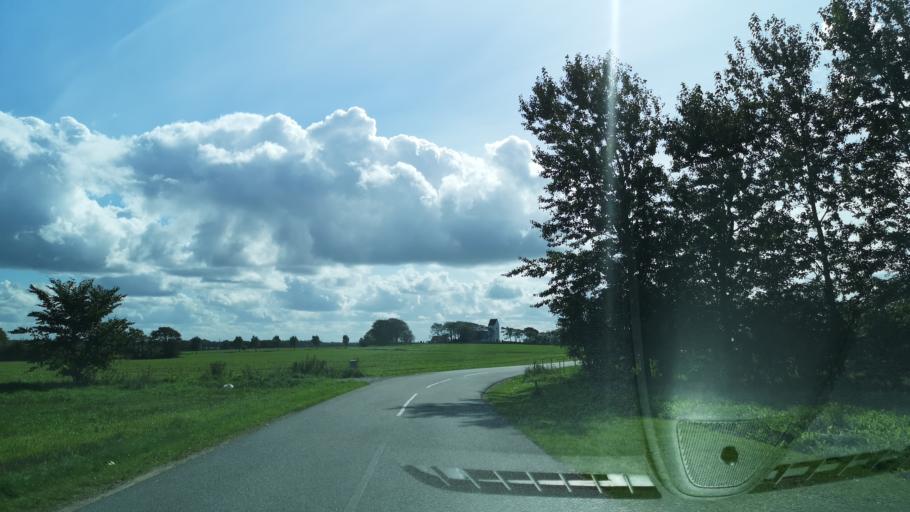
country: DK
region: Central Jutland
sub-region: Ringkobing-Skjern Kommune
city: Skjern
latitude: 55.9810
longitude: 8.5506
